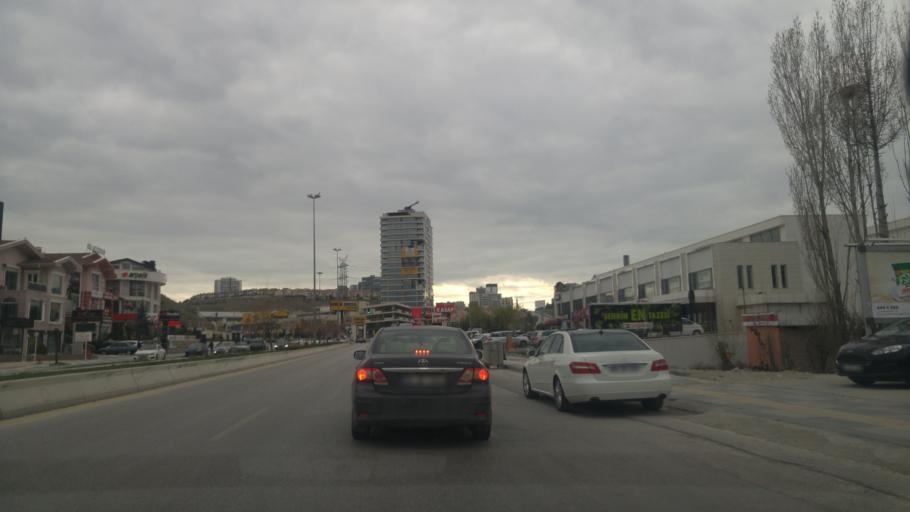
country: TR
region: Ankara
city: Etimesgut
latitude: 39.8614
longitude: 32.6810
